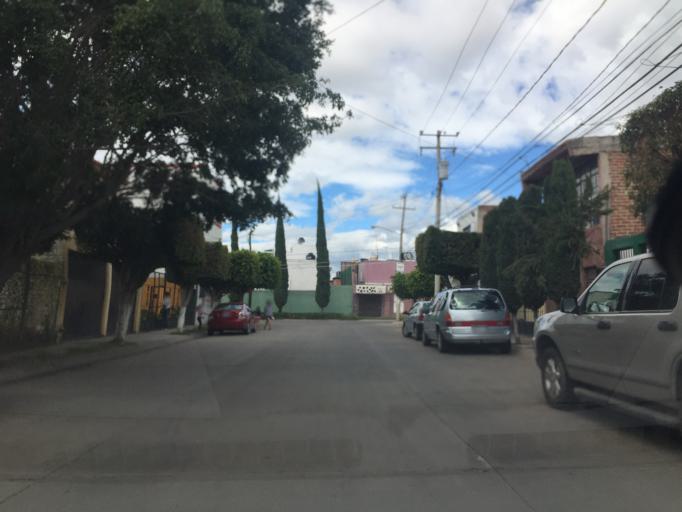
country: MX
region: Guanajuato
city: Leon
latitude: 21.1507
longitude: -101.6569
